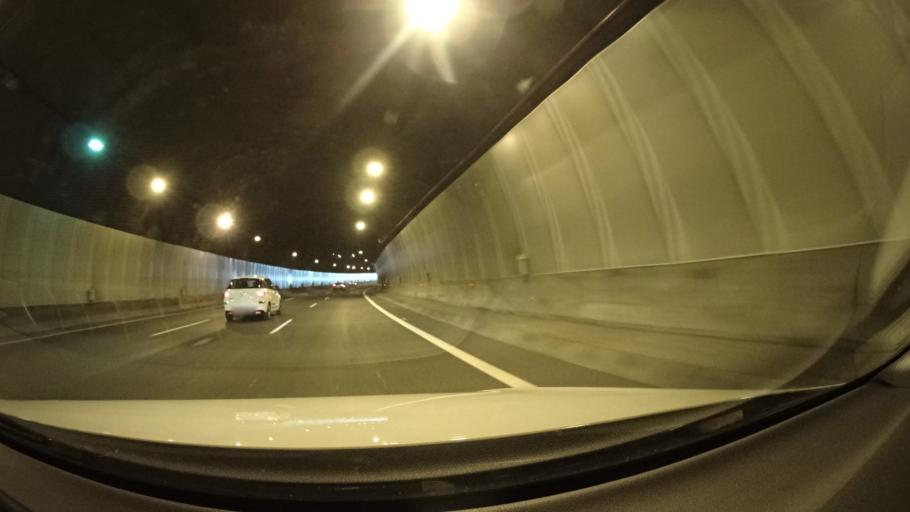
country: ES
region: Canary Islands
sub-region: Provincia de Las Palmas
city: Las Palmas de Gran Canaria
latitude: 28.0537
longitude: -15.4453
